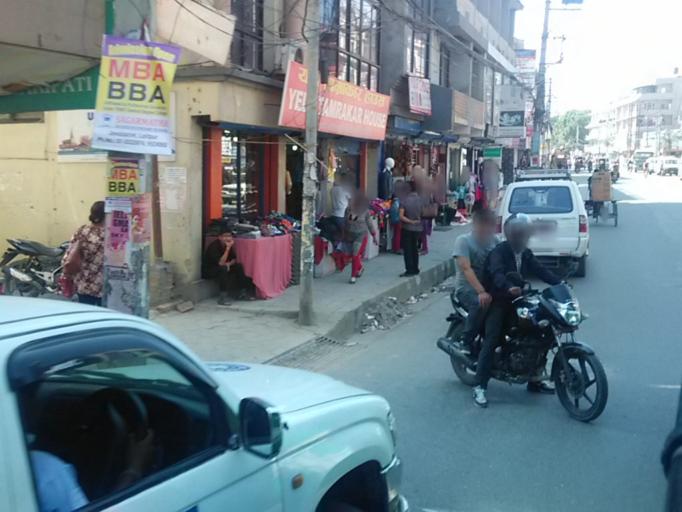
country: NP
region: Central Region
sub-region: Bagmati Zone
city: Patan
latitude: 27.6714
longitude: 85.3189
